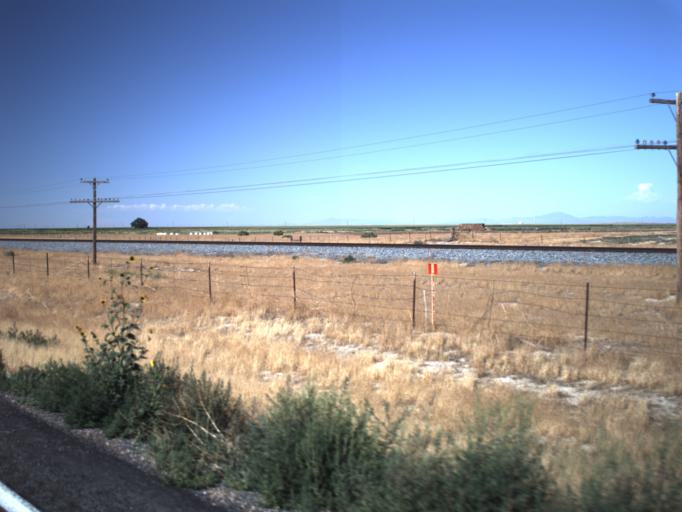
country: US
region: Utah
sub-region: Millard County
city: Delta
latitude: 39.5540
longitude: -112.3543
